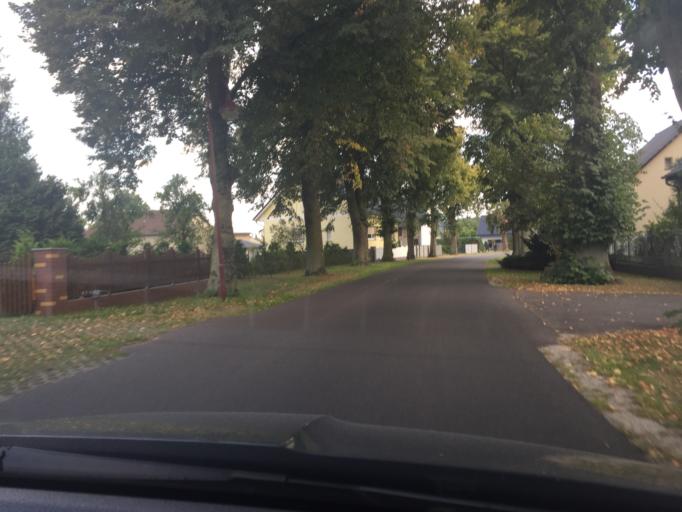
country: DE
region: Brandenburg
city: Spreenhagen
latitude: 52.3540
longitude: 13.8306
